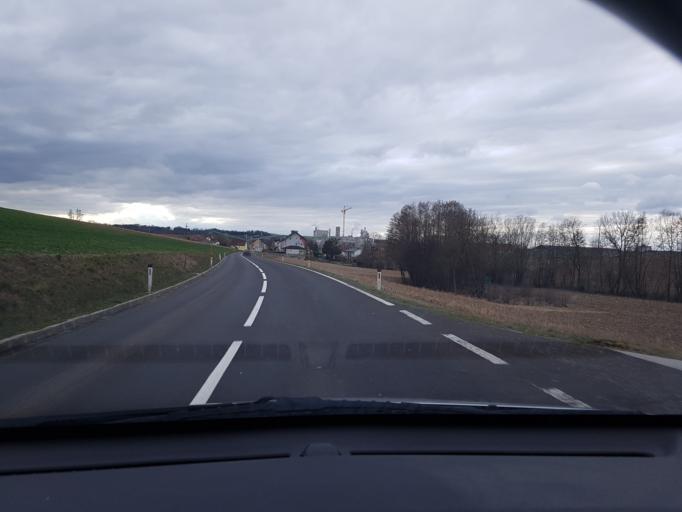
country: AT
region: Upper Austria
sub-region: Politischer Bezirk Linz-Land
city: Ansfelden
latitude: 48.1815
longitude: 14.2694
